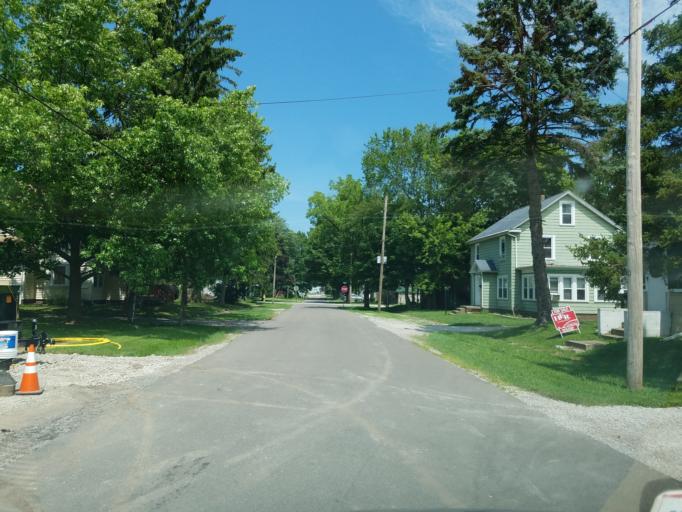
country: US
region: Ohio
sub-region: Ashland County
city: Ashland
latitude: 40.8759
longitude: -82.3274
